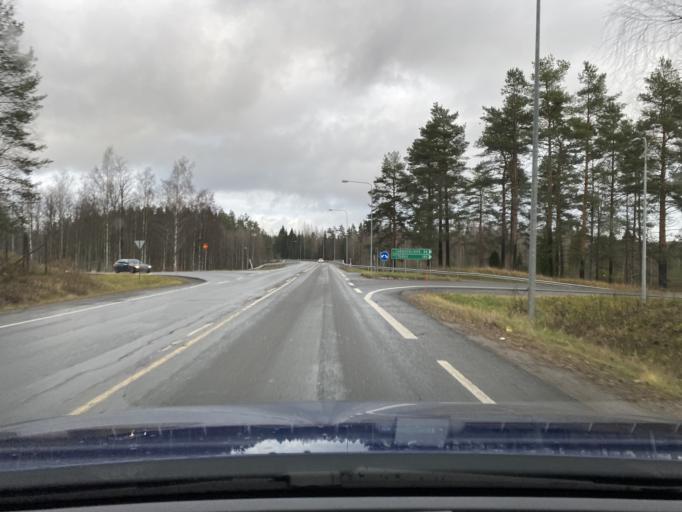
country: FI
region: Pirkanmaa
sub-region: Tampere
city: Lempaeaelae
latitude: 61.3952
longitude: 23.7818
